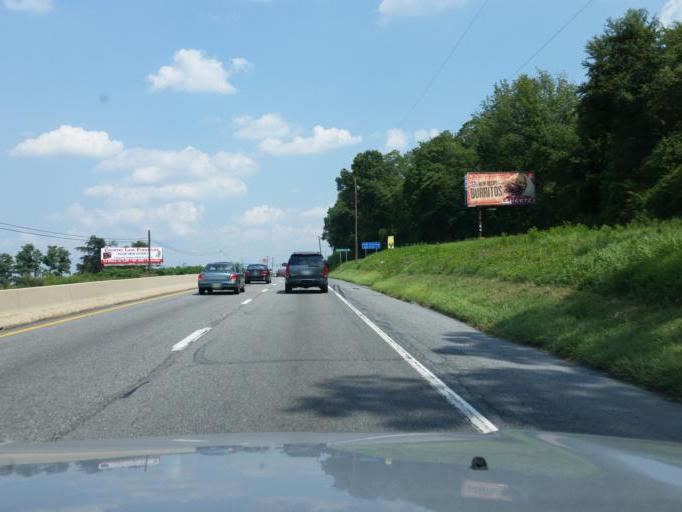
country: US
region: Pennsylvania
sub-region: Dauphin County
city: Rutherford
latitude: 40.2587
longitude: -76.7800
